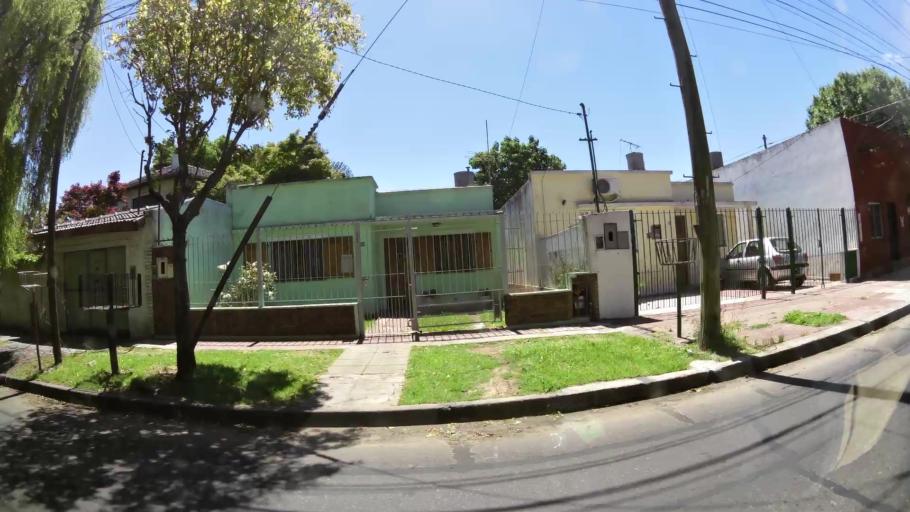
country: AR
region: Buenos Aires
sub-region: Partido de San Isidro
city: San Isidro
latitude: -34.5112
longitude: -58.5711
